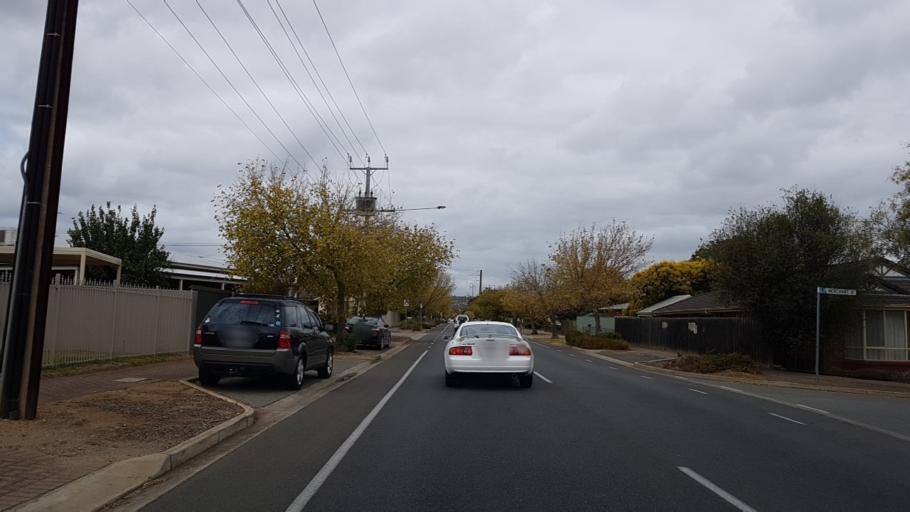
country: AU
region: South Australia
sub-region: Marion
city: Clovelly Park
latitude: -35.0056
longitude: 138.5657
